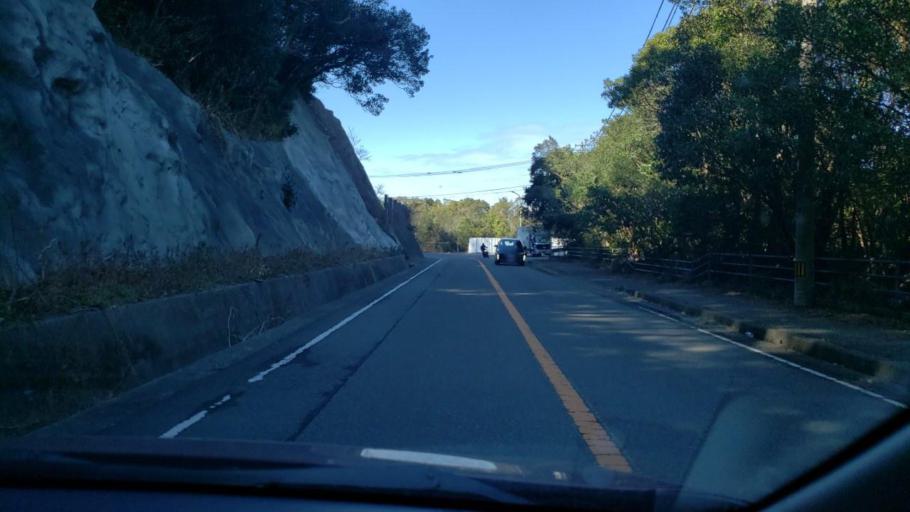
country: JP
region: Tokushima
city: Narutocho-mitsuishi
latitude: 34.2207
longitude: 134.5734
